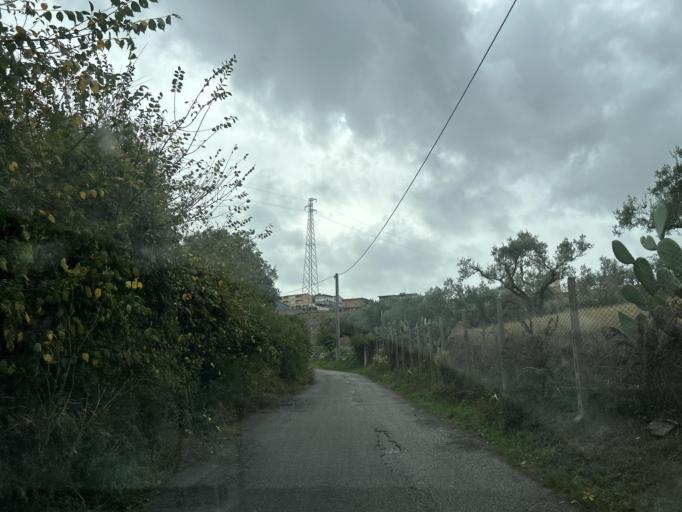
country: IT
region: Calabria
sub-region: Provincia di Catanzaro
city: Staletti
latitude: 38.7682
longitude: 16.5318
